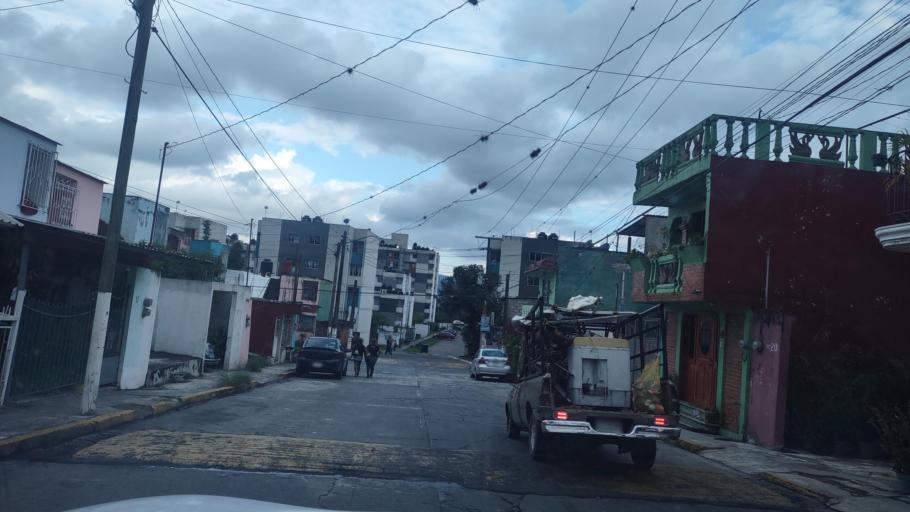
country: MX
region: Veracruz
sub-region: Ixtaczoquitlan
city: Buenavista
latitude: 18.8830
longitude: -97.0631
